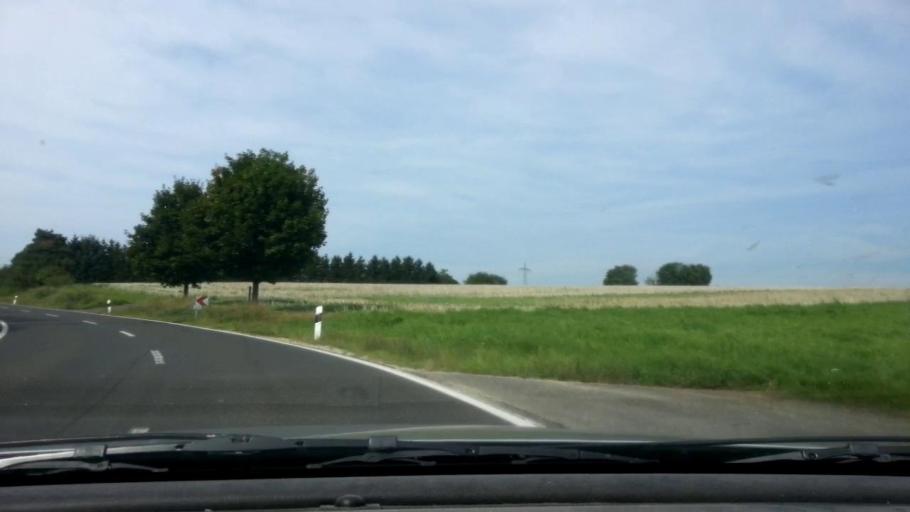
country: DE
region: Bavaria
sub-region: Upper Franconia
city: Memmelsdorf
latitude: 49.9520
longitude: 10.9568
